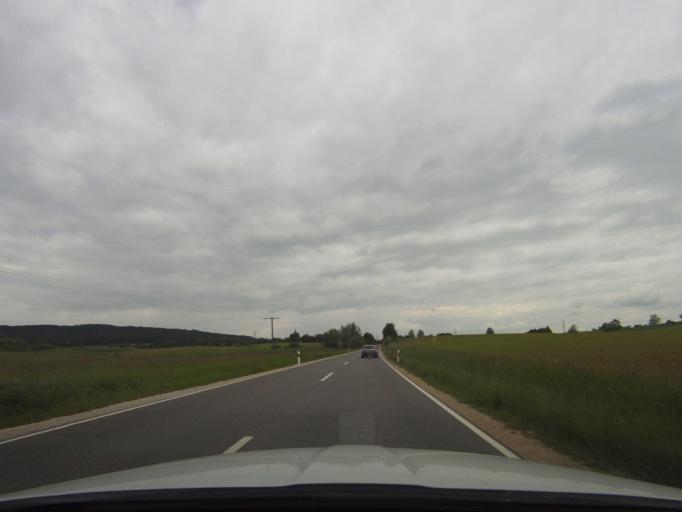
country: DE
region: Bavaria
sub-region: Upper Franconia
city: Altendorf
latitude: 50.1071
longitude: 11.1747
